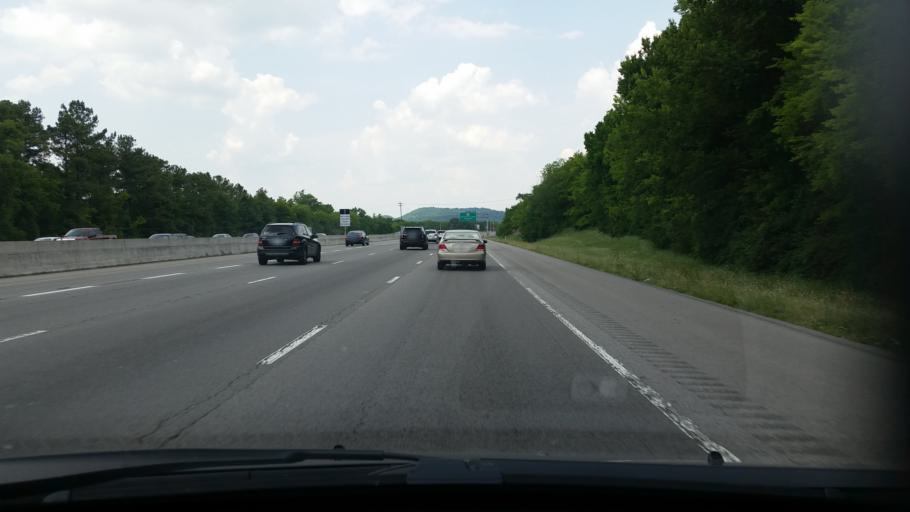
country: US
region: Tennessee
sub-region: Williamson County
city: Brentwood Estates
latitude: 36.0175
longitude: -86.7862
